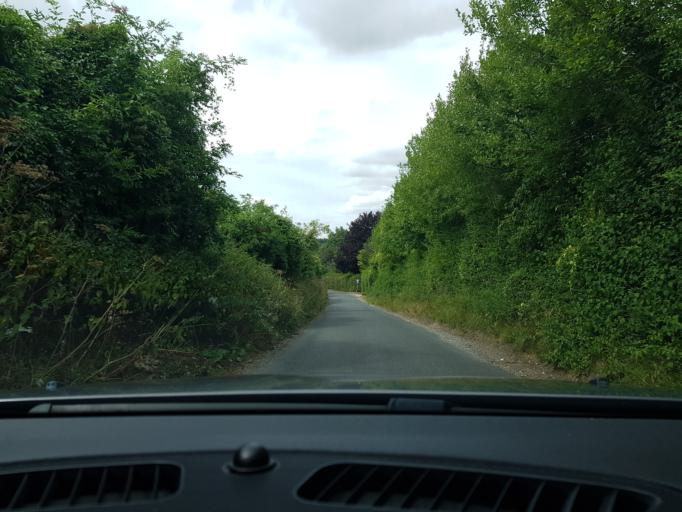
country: GB
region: England
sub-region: West Berkshire
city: Kintbury
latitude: 51.4215
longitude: -1.4670
